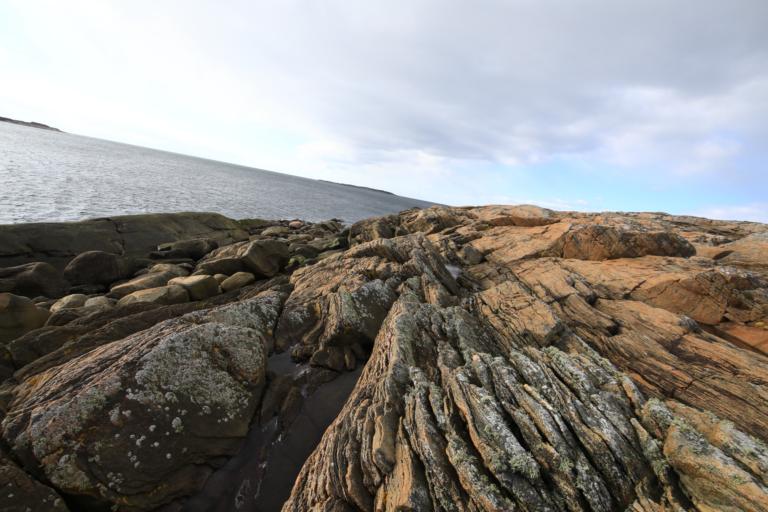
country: SE
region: Halland
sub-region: Kungsbacka Kommun
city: Frillesas
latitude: 57.2165
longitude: 12.1342
